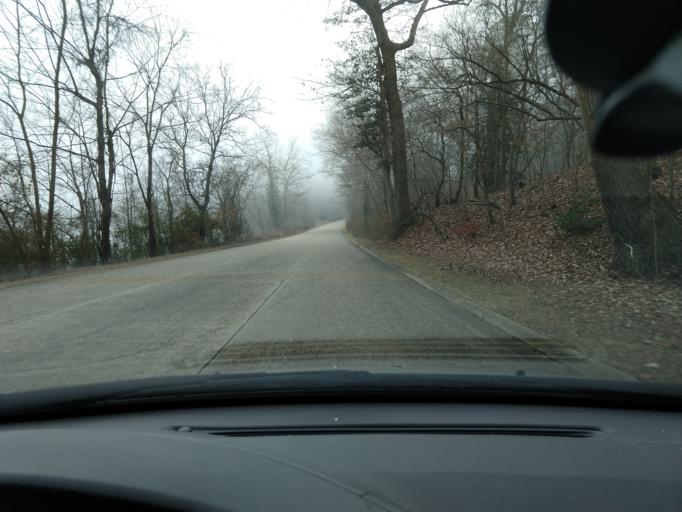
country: US
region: Virginia
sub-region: York County
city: Yorktown
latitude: 37.2439
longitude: -76.5271
